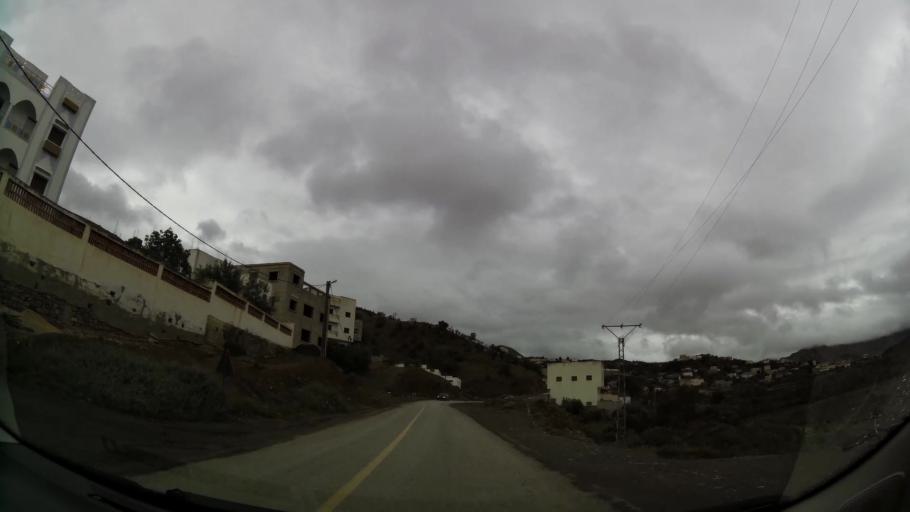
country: MA
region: Taza-Al Hoceima-Taounate
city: Imzourene
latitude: 34.9589
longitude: -3.8106
